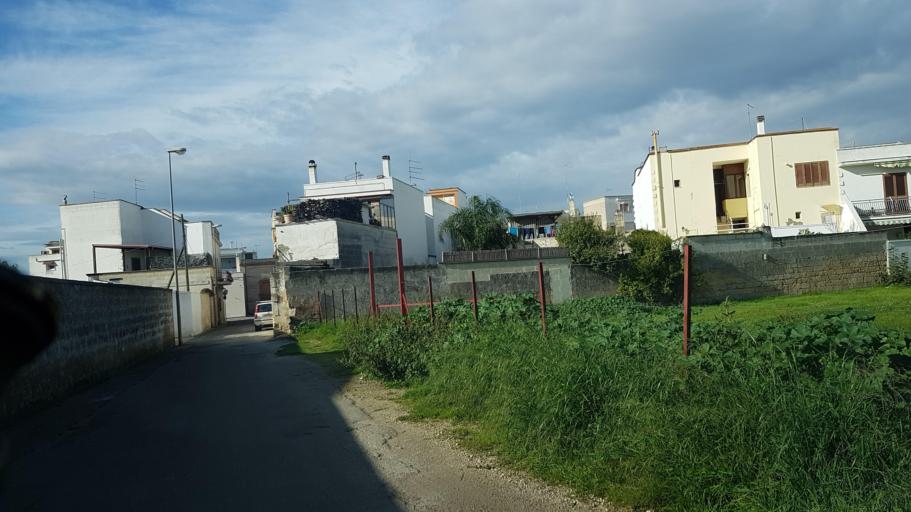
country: IT
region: Apulia
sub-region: Provincia di Brindisi
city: Torre Santa Susanna
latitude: 40.4665
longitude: 17.7436
